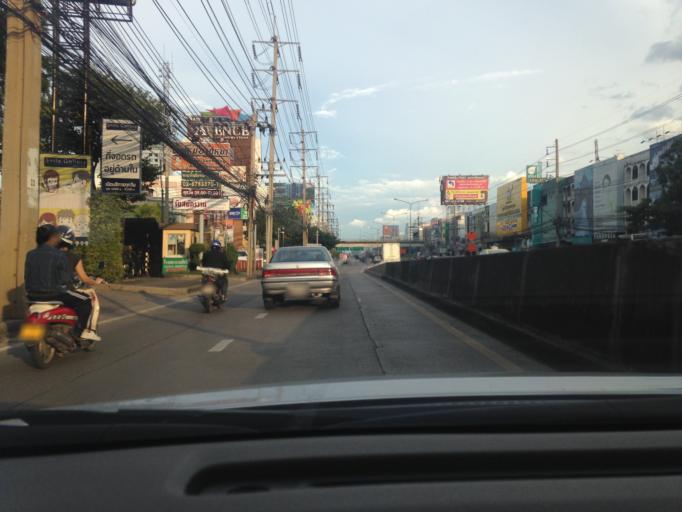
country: TH
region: Bangkok
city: Lak Si
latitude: 13.8942
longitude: 100.5579
